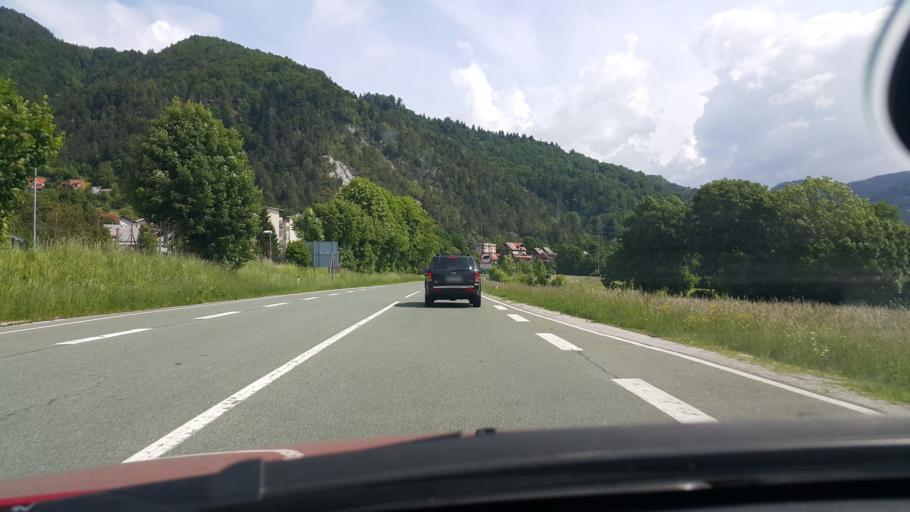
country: SI
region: Trzic
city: Bistrica pri Trzicu
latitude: 46.3552
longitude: 14.2935
